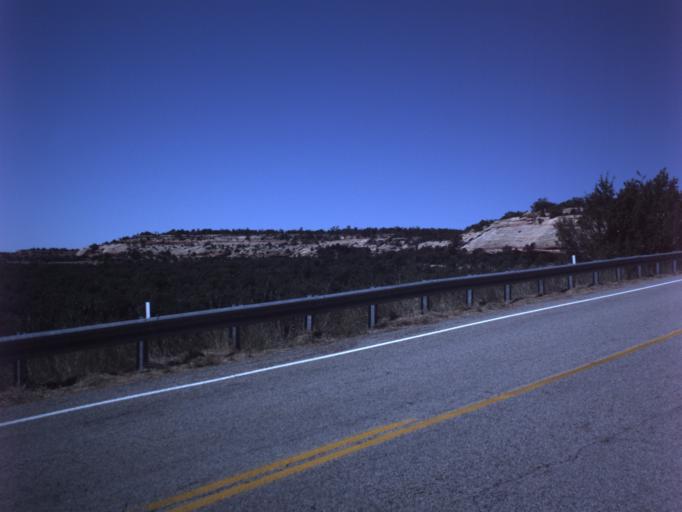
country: US
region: Utah
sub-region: San Juan County
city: Blanding
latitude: 37.5507
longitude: -109.7743
